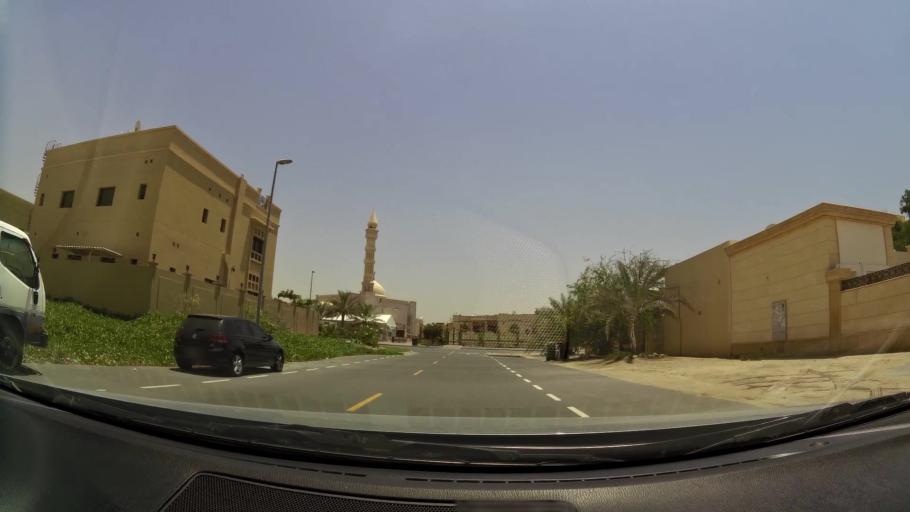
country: AE
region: Dubai
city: Dubai
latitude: 25.0983
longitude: 55.1963
